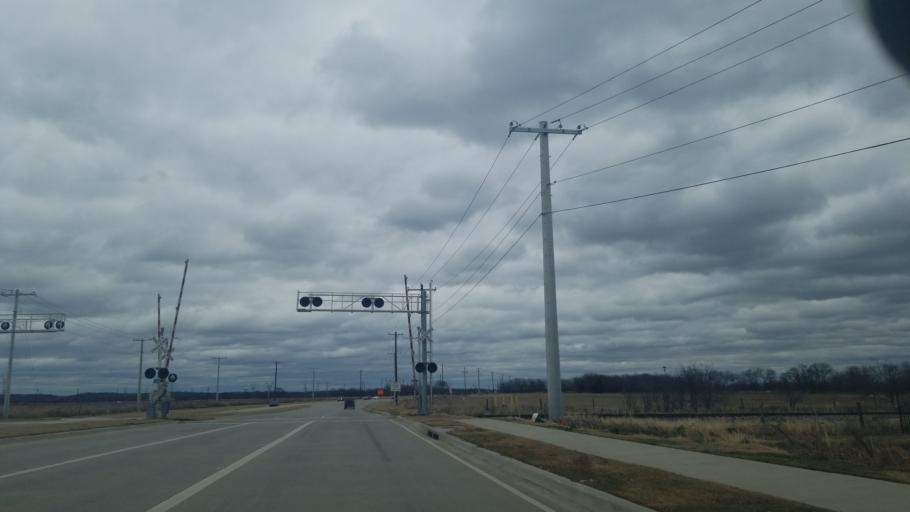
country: US
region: Texas
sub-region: Denton County
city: Roanoke
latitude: 33.0580
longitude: -97.2092
